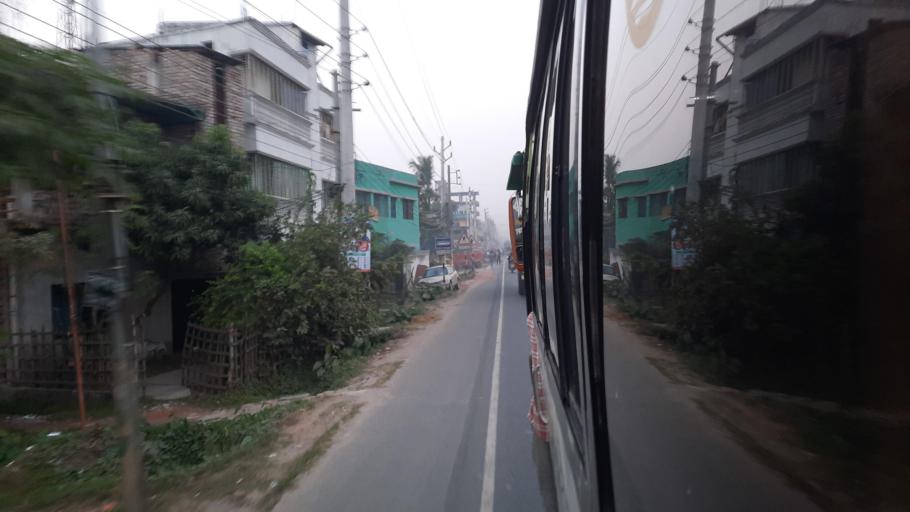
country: BD
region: Khulna
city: Jessore
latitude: 23.1702
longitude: 89.1927
